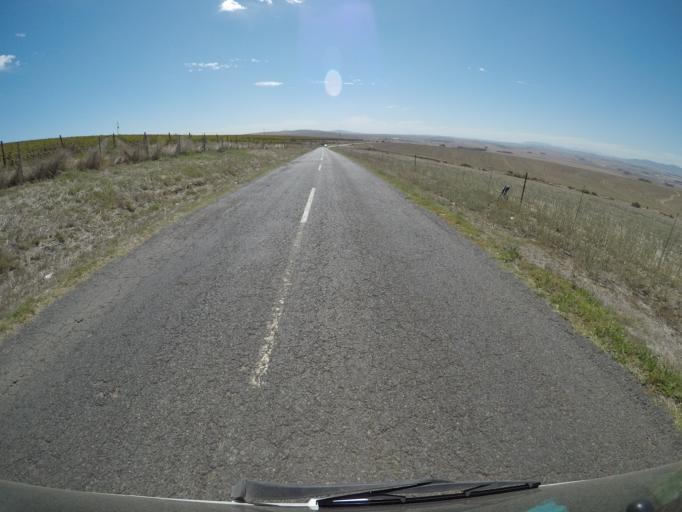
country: ZA
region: Western Cape
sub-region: City of Cape Town
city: Sunset Beach
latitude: -33.7142
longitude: 18.5825
